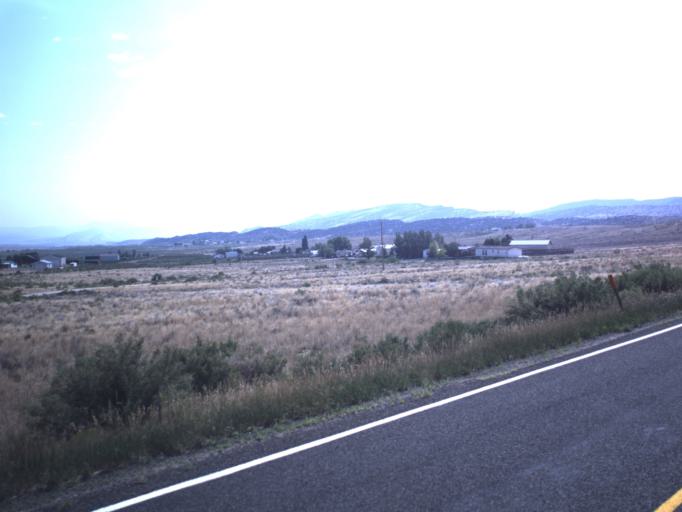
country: US
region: Utah
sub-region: Daggett County
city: Manila
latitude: 40.9730
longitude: -109.7190
